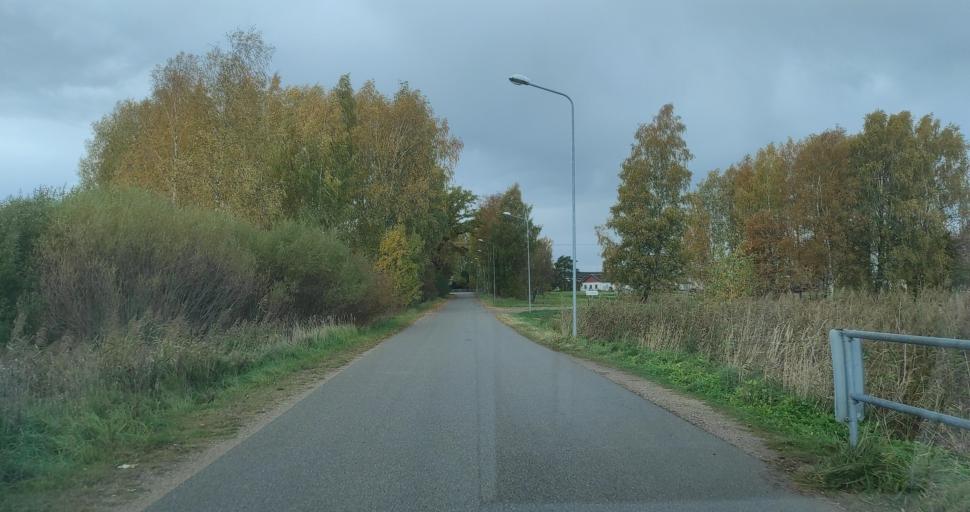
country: LV
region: Skrunda
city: Skrunda
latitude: 56.6852
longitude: 22.0049
